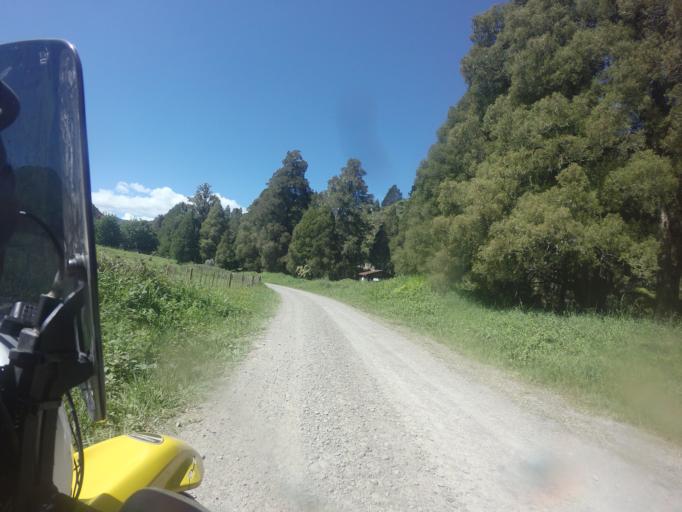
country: NZ
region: Bay of Plenty
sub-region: Opotiki District
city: Opotiki
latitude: -38.2961
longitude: 177.3369
